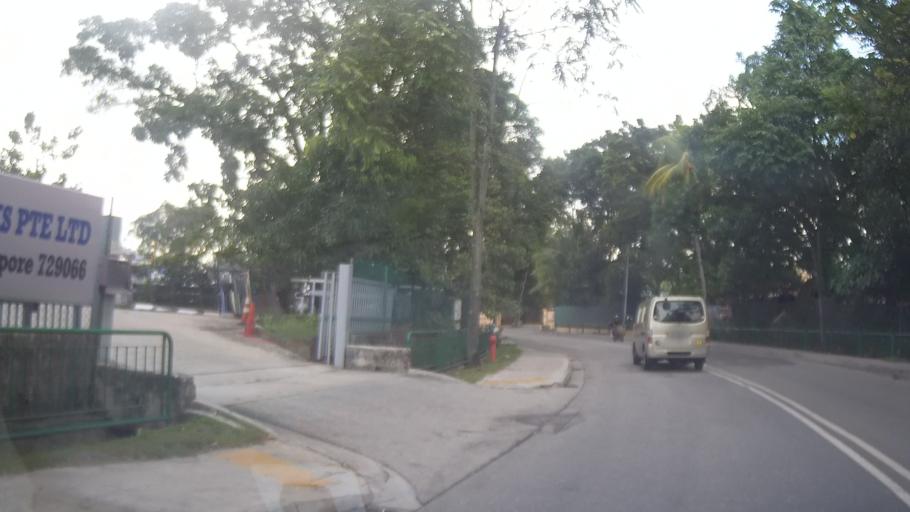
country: MY
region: Johor
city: Johor Bahru
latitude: 1.4211
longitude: 103.7459
